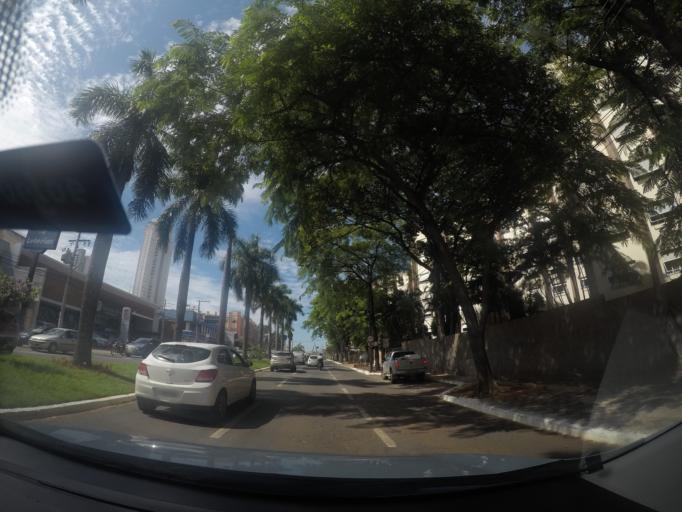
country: BR
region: Goias
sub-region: Goiania
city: Goiania
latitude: -16.7030
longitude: -49.2643
